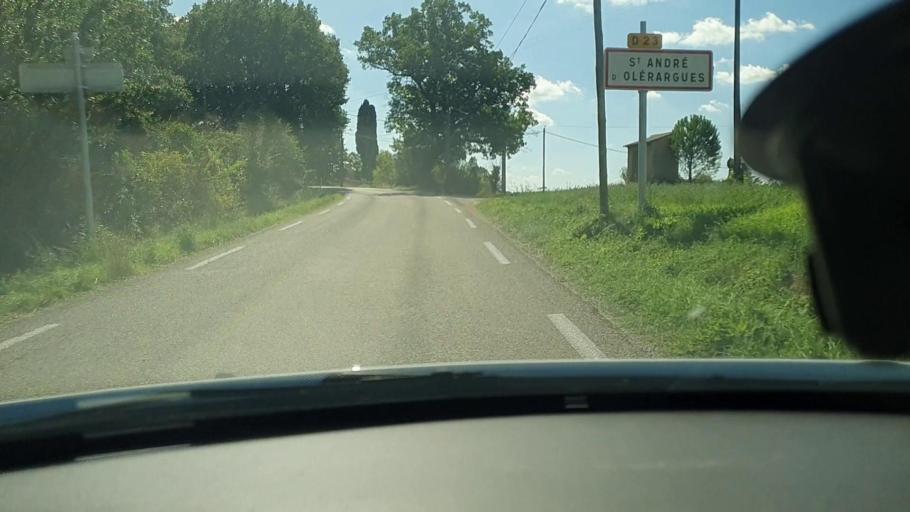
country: FR
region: Languedoc-Roussillon
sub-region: Departement du Gard
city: Goudargues
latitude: 44.1667
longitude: 4.4841
